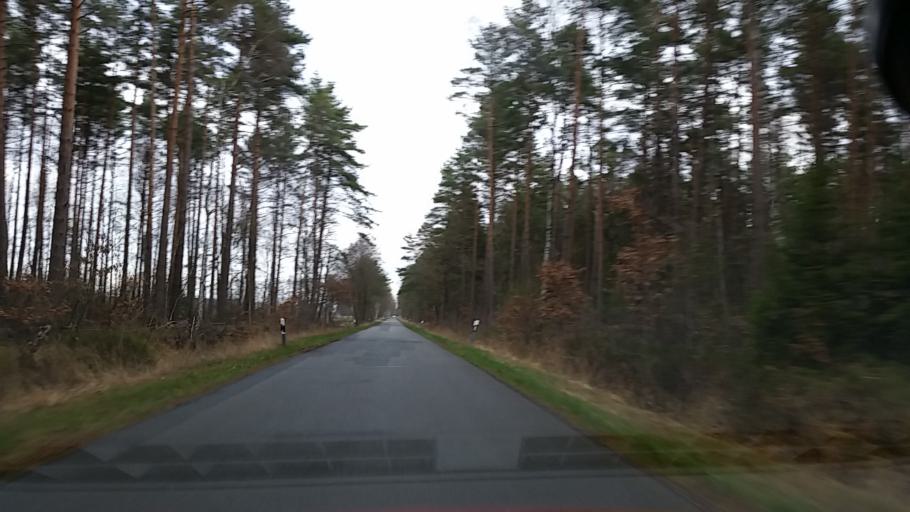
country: DE
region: Lower Saxony
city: Luder
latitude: 52.7820
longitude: 10.6683
